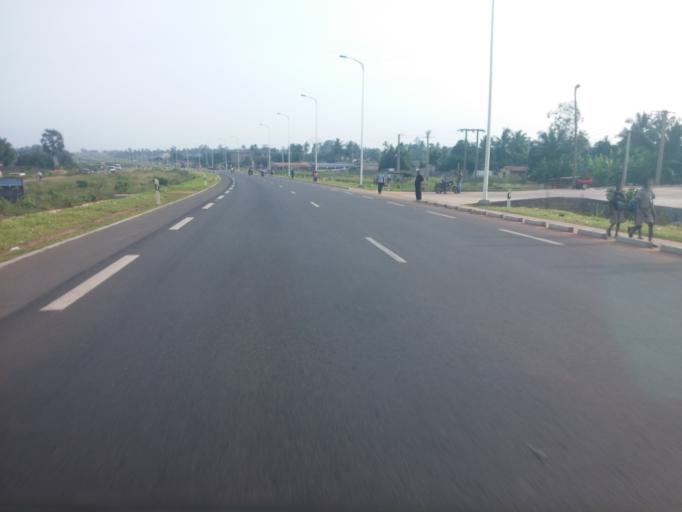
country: TG
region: Maritime
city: Tsevie
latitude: 6.3260
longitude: 1.2186
